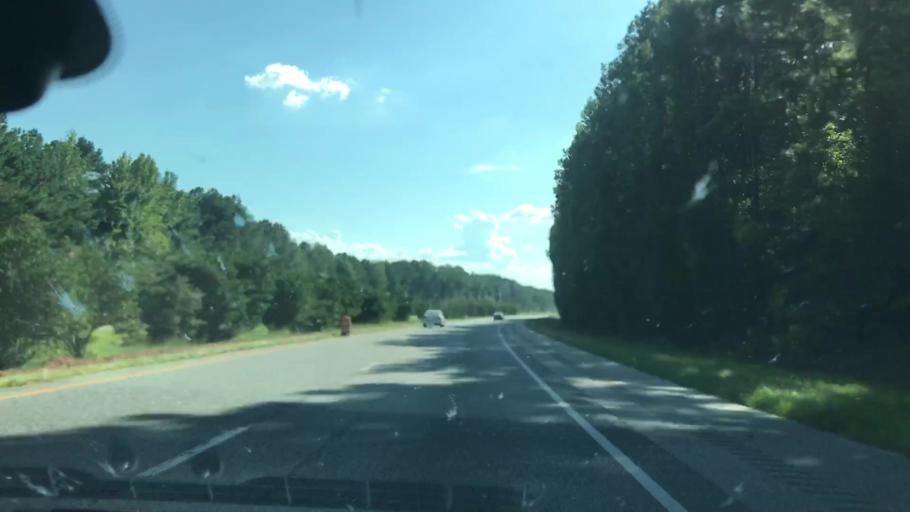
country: US
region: Georgia
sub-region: Harris County
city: Hamilton
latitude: 32.8328
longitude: -85.0051
